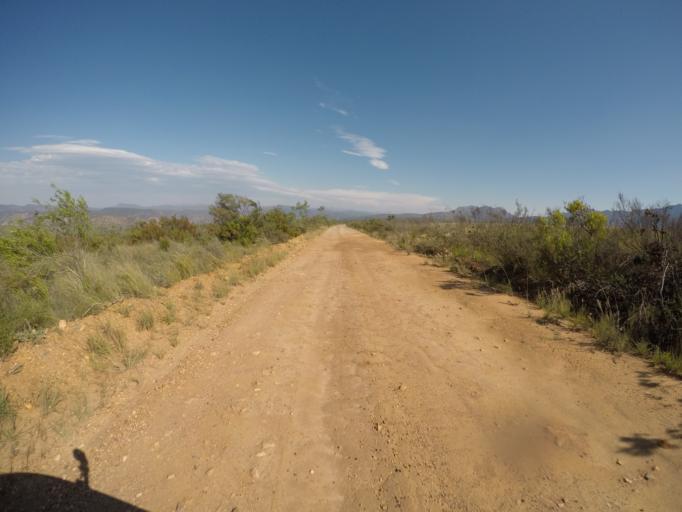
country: ZA
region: Eastern Cape
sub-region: Cacadu District Municipality
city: Kareedouw
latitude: -33.6351
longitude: 24.4689
